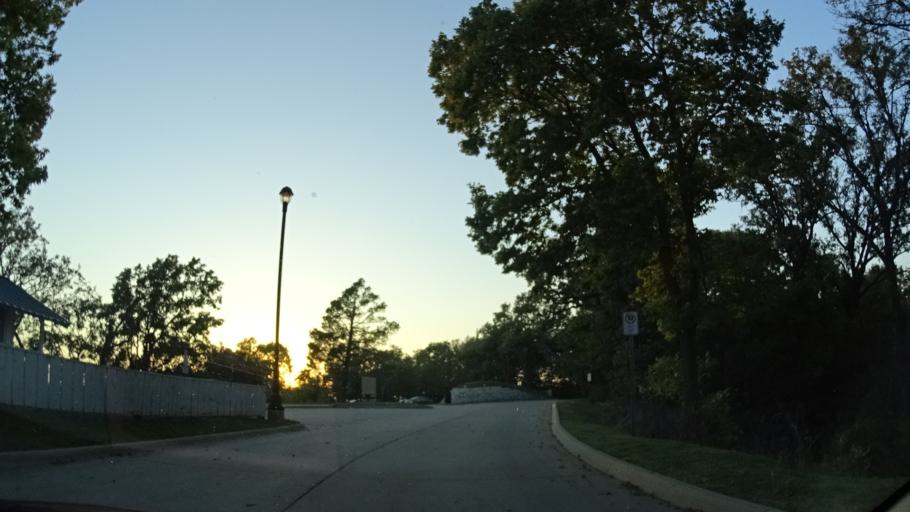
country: US
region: Iowa
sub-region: Pottawattamie County
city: Council Bluffs
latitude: 41.3034
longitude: -95.8566
